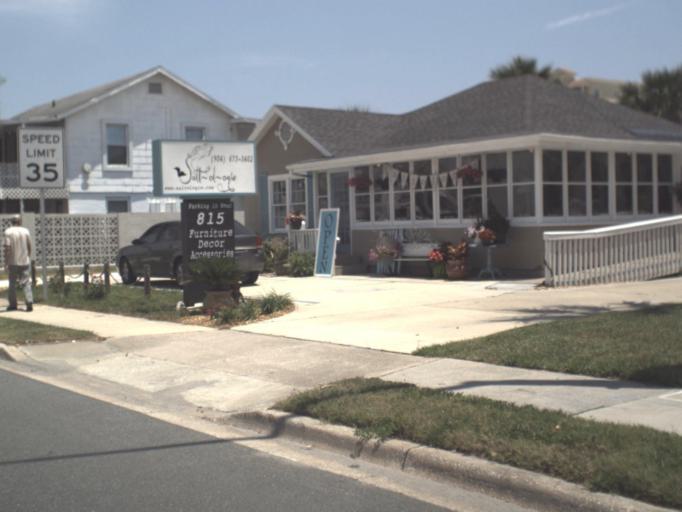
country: US
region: Florida
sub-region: Duval County
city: Jacksonville Beach
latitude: 30.2958
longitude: -81.3932
